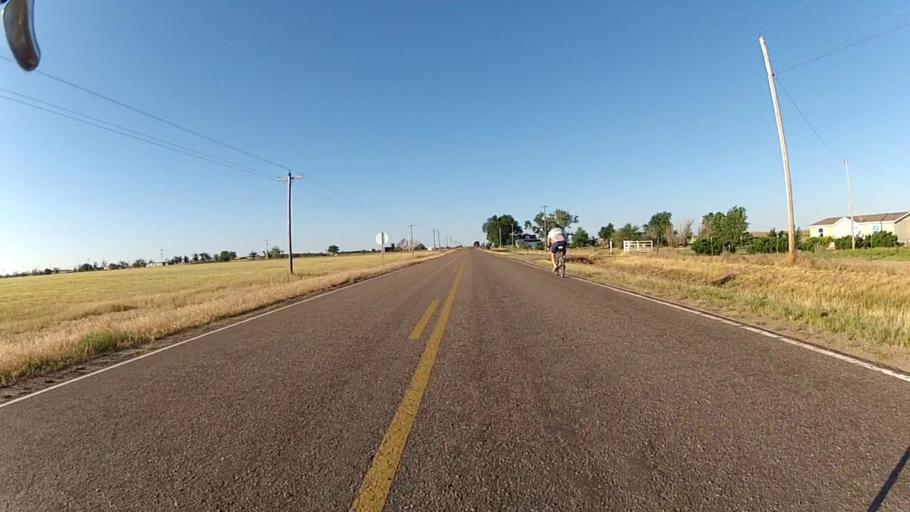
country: US
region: Kansas
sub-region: Ford County
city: Dodge City
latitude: 37.7042
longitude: -99.9064
